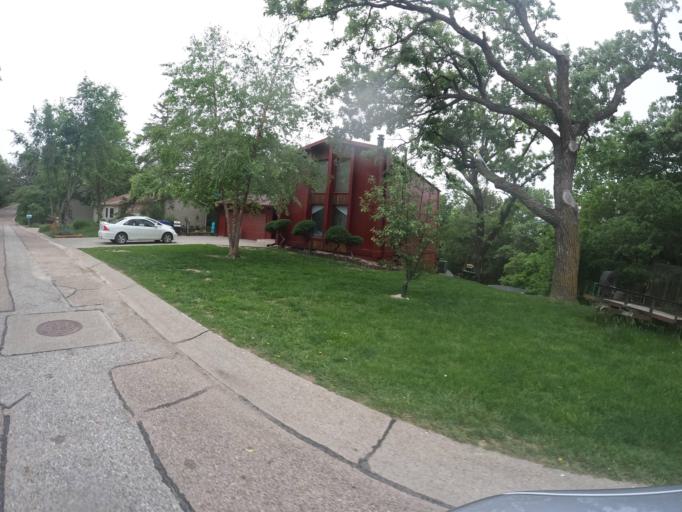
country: US
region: Nebraska
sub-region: Sarpy County
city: Offutt Air Force Base
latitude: 41.0535
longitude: -95.9698
